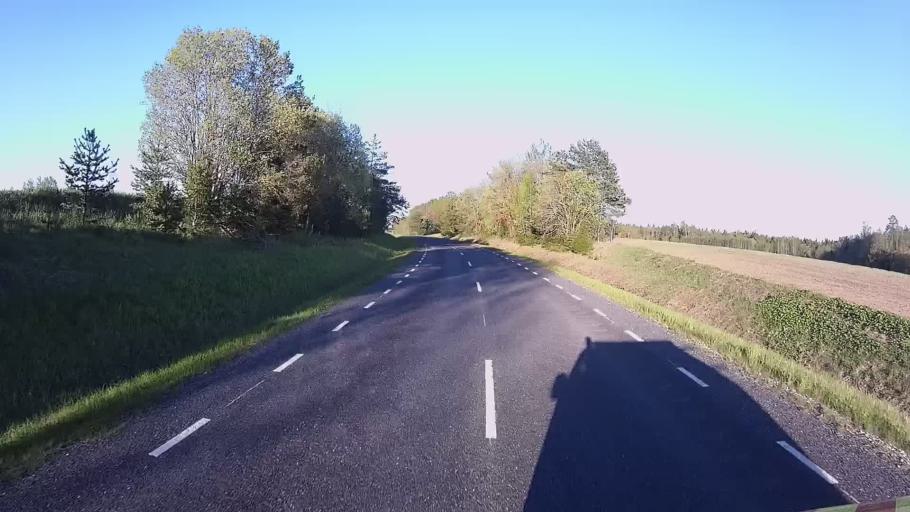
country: EE
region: Jogevamaa
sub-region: Poltsamaa linn
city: Poltsamaa
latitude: 58.5218
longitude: 25.9717
